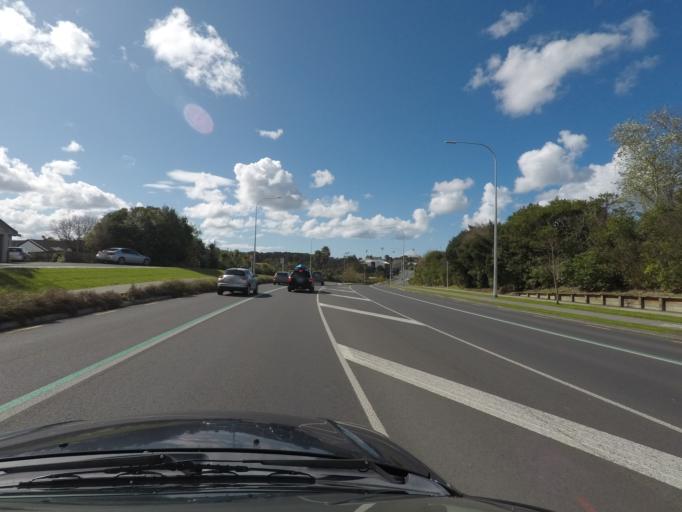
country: NZ
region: Auckland
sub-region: Auckland
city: Rothesay Bay
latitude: -36.7335
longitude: 174.6921
